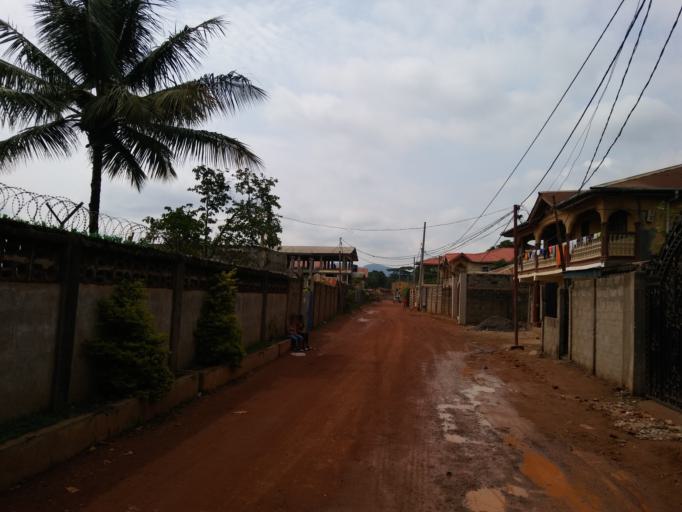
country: SL
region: Western Area
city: Hastings
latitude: 8.3889
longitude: -13.1471
